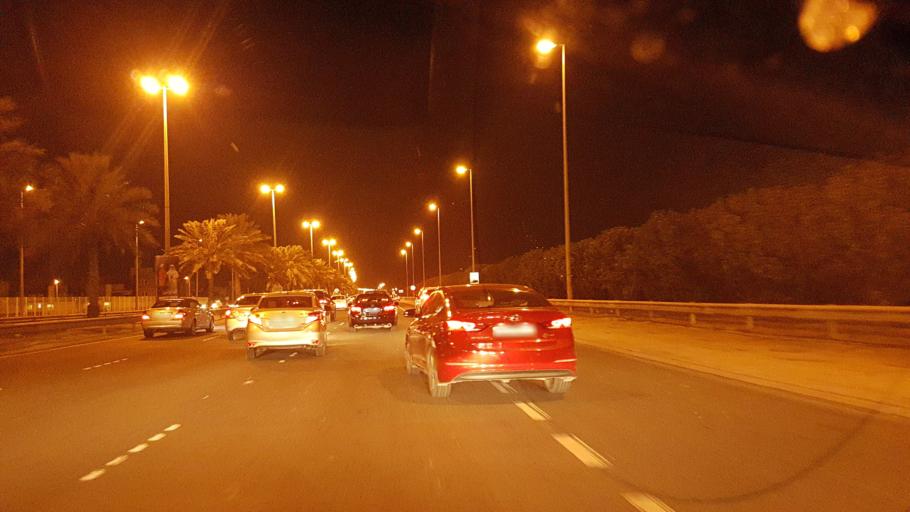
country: BH
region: Central Governorate
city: Madinat Hamad
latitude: 26.1478
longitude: 50.5094
